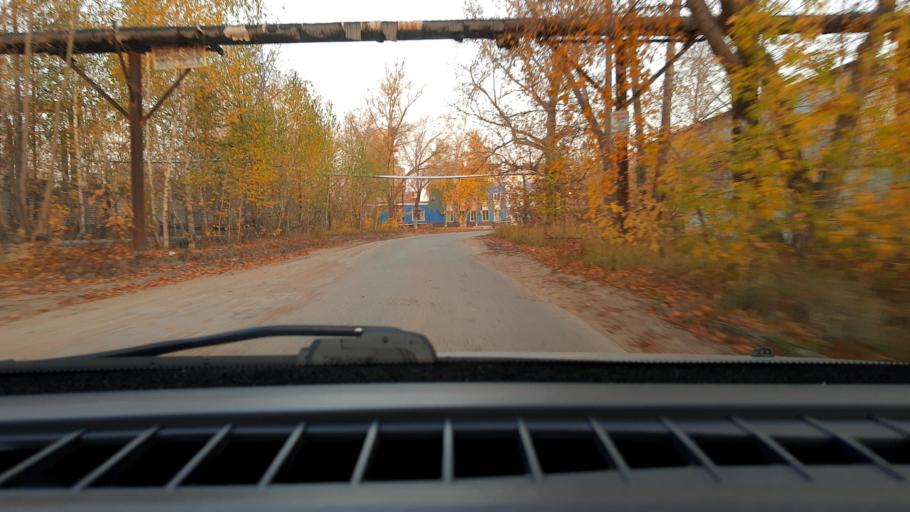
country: RU
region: Nizjnij Novgorod
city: Gorbatovka
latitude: 56.3744
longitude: 43.7897
